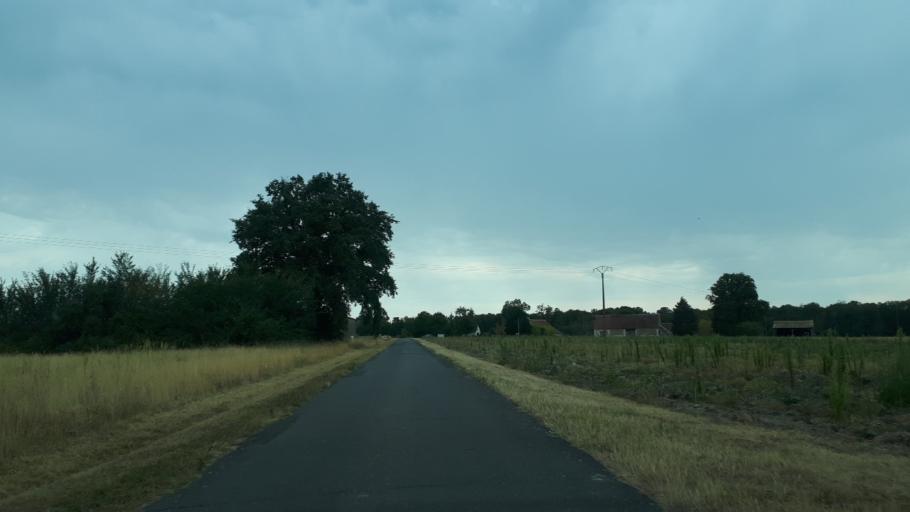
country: FR
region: Centre
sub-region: Departement du Loir-et-Cher
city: Saint-Romain-sur-Cher
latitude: 47.3568
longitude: 1.4009
